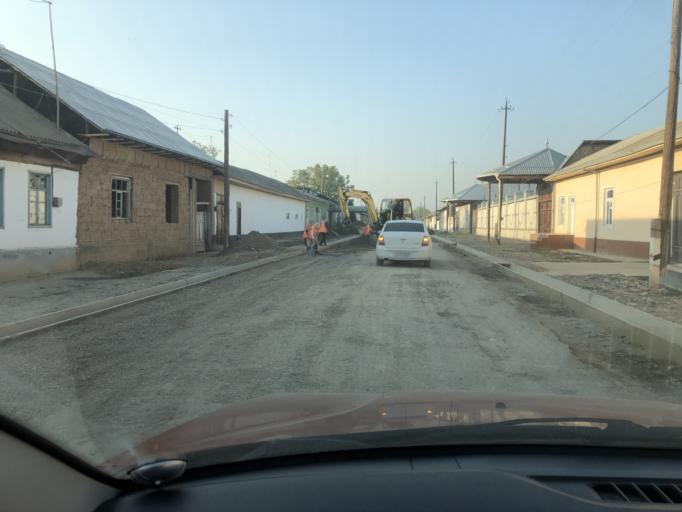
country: UZ
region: Namangan
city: Uychi
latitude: 41.0769
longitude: 72.0025
